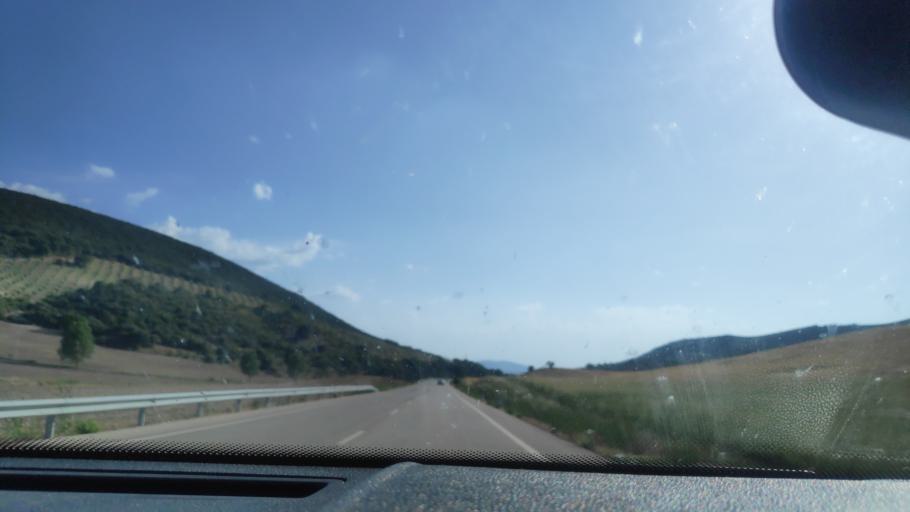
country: ES
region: Andalusia
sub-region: Provincia de Granada
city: Campotejar
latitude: 37.4677
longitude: -3.5893
